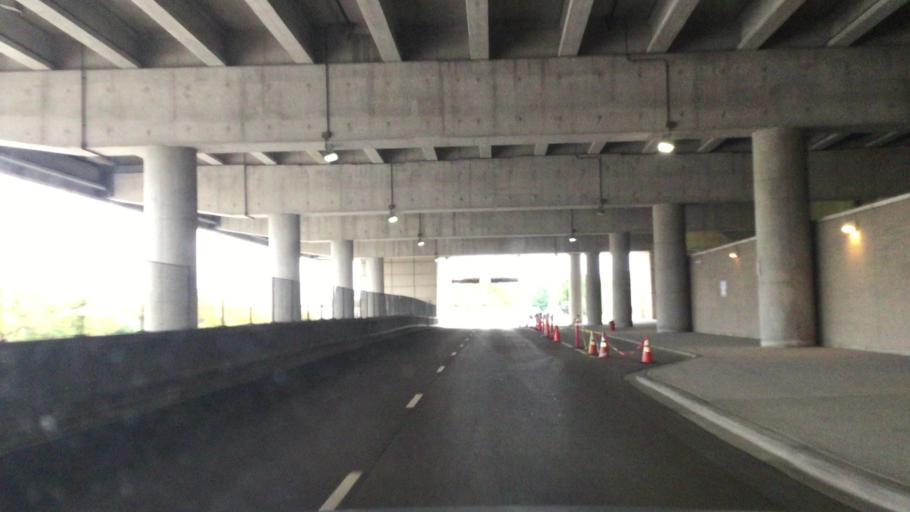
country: US
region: Illinois
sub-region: Cook County
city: Chicago
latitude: 41.8485
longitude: -87.6206
